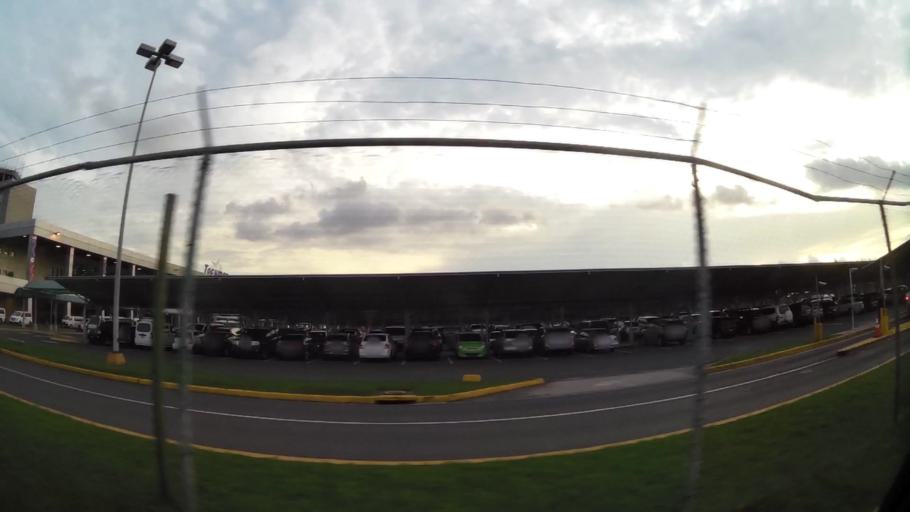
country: PA
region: Panama
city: Tocumen
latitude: 9.0683
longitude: -79.3875
